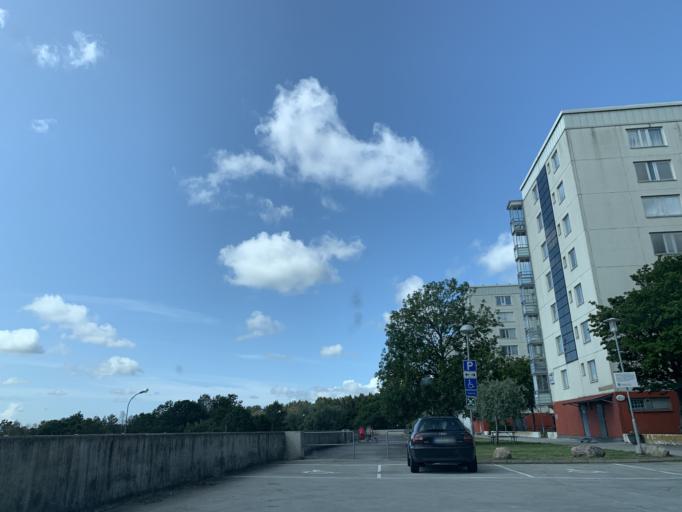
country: SE
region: Vaestra Goetaland
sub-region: Goteborg
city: Hammarkullen
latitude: 57.7722
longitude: 12.0283
